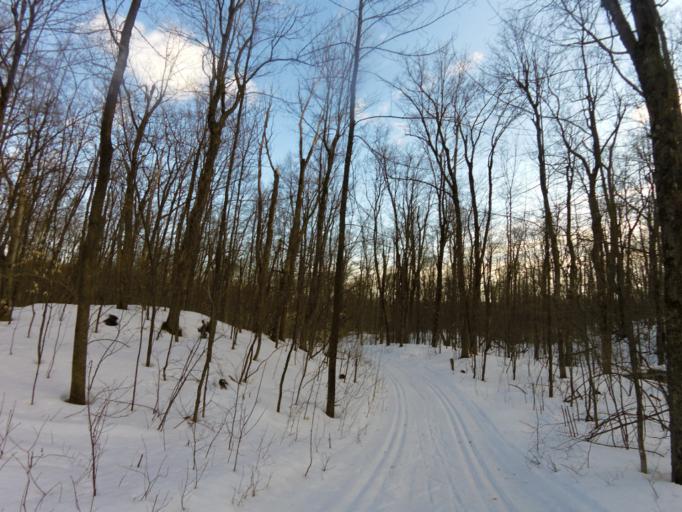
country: CA
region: Quebec
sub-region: Outaouais
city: Gatineau
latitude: 45.4740
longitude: -75.8391
